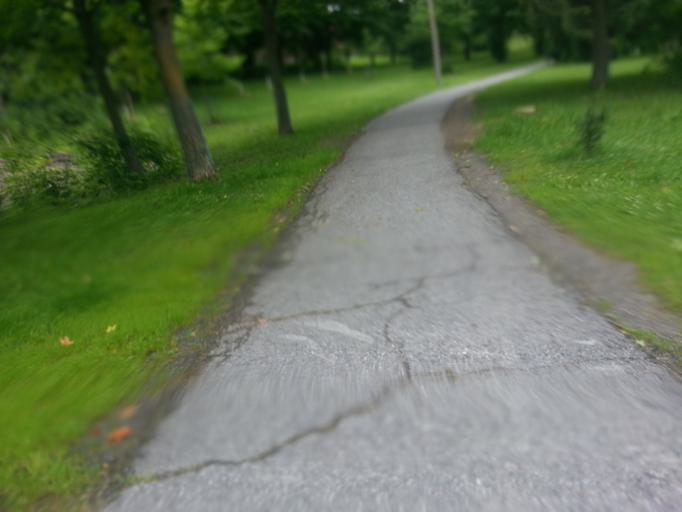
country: CA
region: Ontario
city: Bells Corners
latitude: 45.3322
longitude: -75.9176
